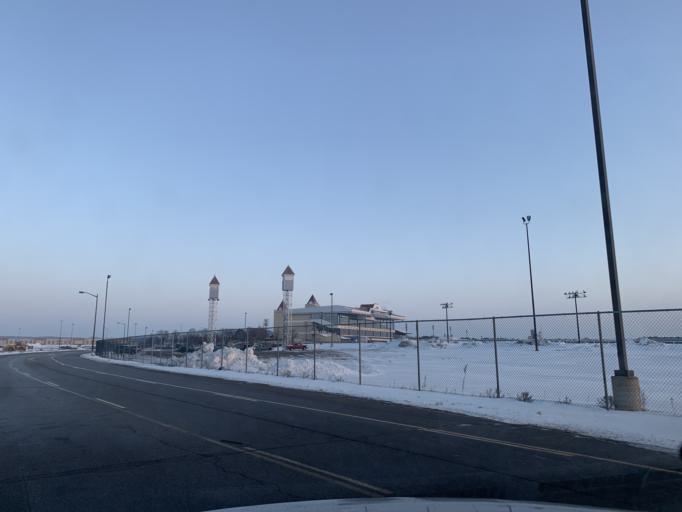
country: US
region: Minnesota
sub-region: Scott County
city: Shakopee
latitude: 44.7871
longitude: -93.4844
